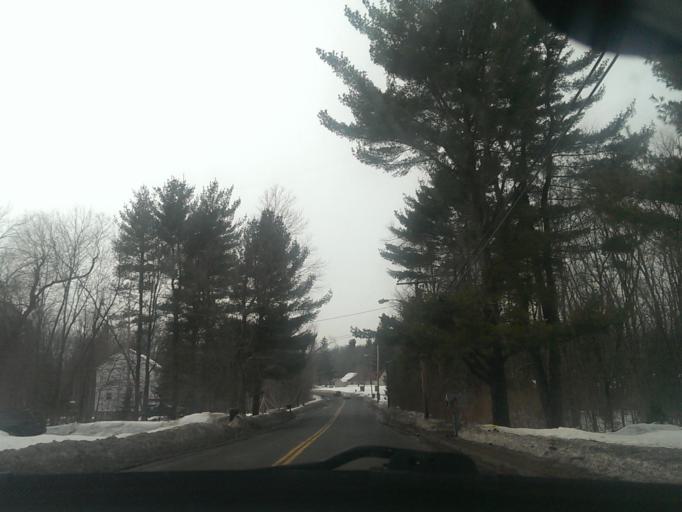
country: US
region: Massachusetts
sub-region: Hampden County
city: East Longmeadow
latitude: 42.0860
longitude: -72.4789
